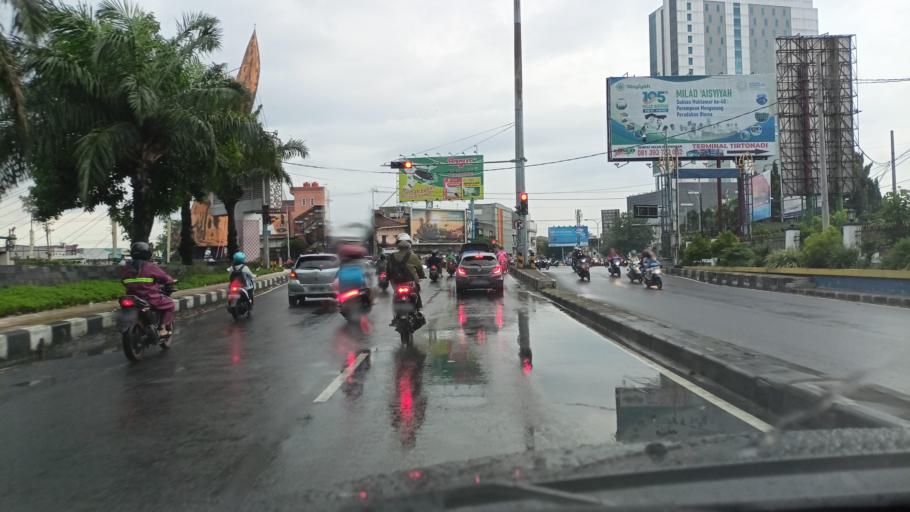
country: ID
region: Central Java
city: Surakarta
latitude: -7.5518
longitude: 110.8207
